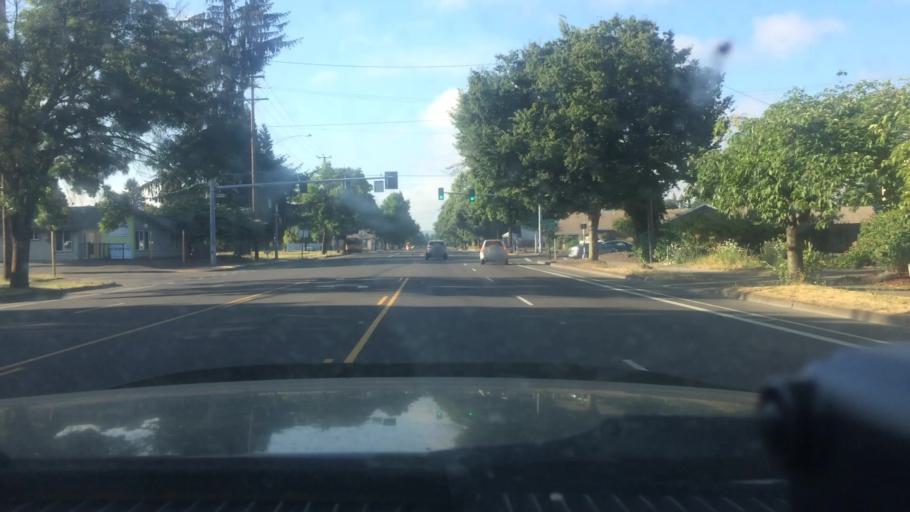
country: US
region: Oregon
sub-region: Lane County
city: Eugene
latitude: 44.0887
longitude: -123.1252
